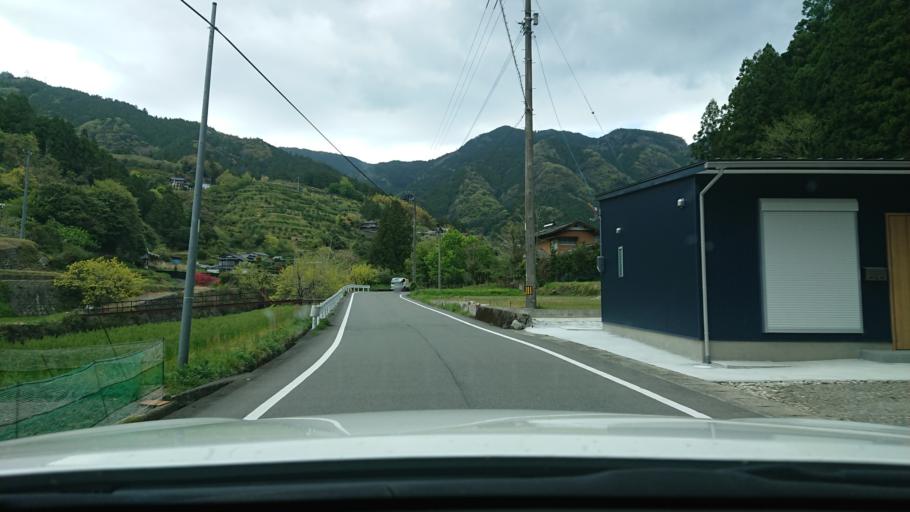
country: JP
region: Tokushima
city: Ishii
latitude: 33.9235
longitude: 134.4238
